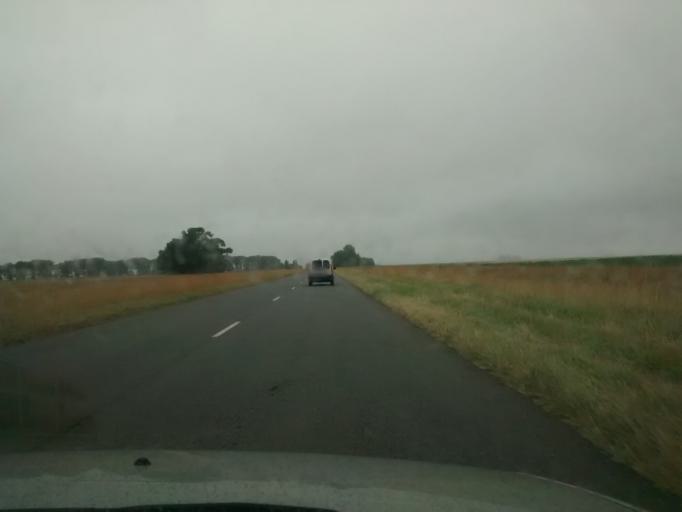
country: AR
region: Buenos Aires
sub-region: Partido de Ayacucho
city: Ayacucho
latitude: -37.4709
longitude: -58.4783
